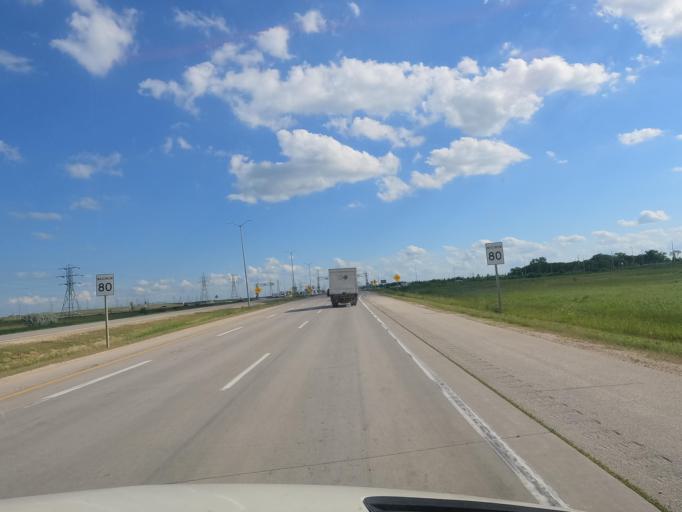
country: CA
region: Manitoba
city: Winnipeg
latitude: 49.8892
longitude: -96.9591
